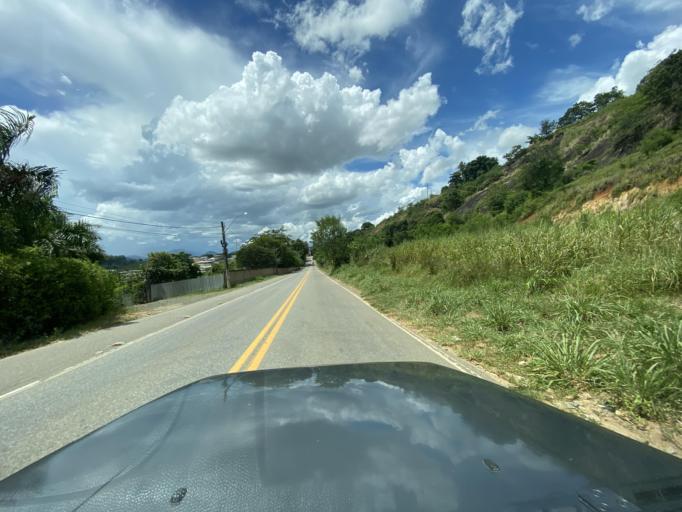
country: BR
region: Espirito Santo
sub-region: Jeronimo Monteiro
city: Jeronimo Monteiro
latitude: -20.7931
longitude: -41.3966
